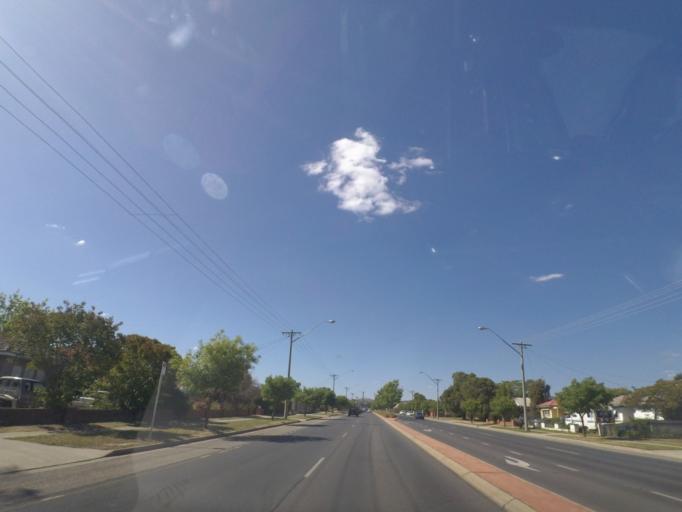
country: AU
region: New South Wales
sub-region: Albury Municipality
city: North Albury
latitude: -36.0564
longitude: 146.9328
